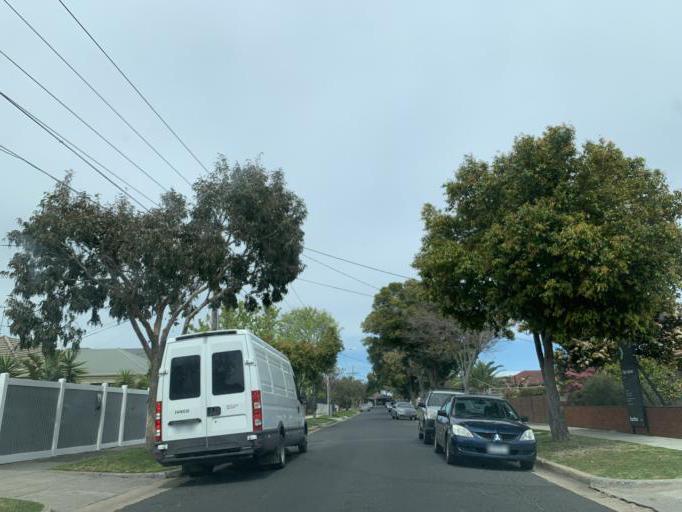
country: AU
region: Victoria
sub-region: Bayside
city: Hampton East
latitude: -37.9490
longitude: 145.0267
